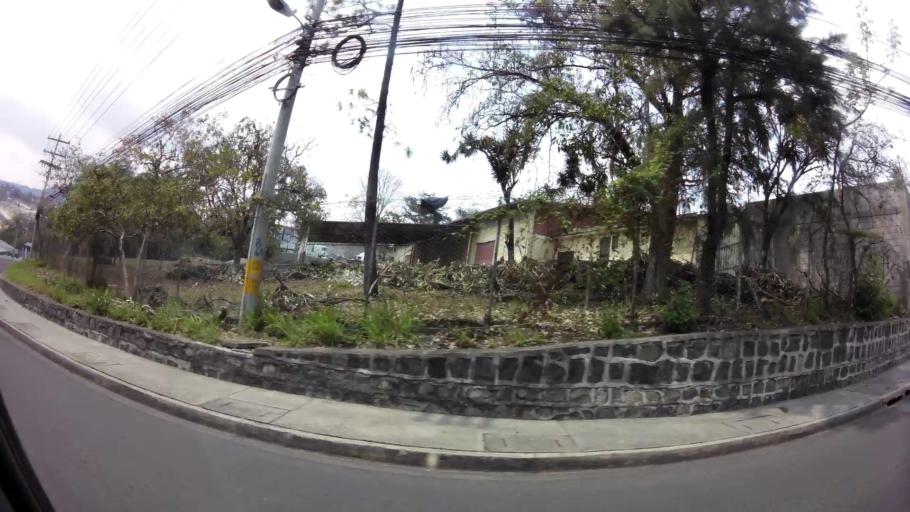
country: HN
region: Francisco Morazan
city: Tegucigalpa
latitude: 14.0580
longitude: -87.2308
